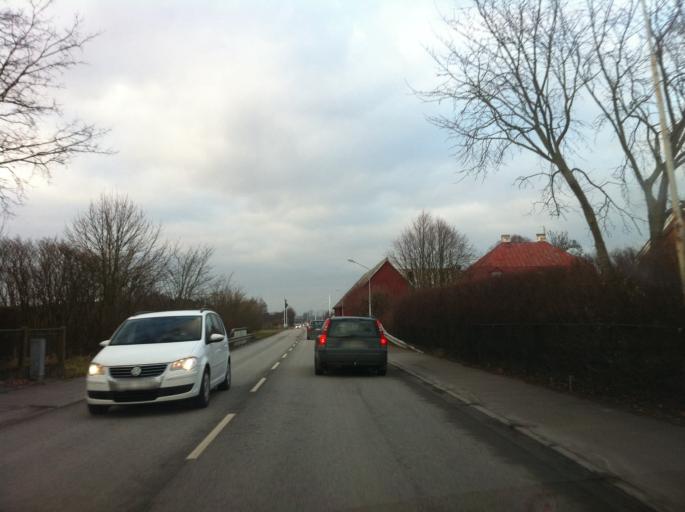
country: SE
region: Skane
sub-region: Kavlinge Kommun
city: Loddekopinge
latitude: 55.7622
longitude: 13.0154
